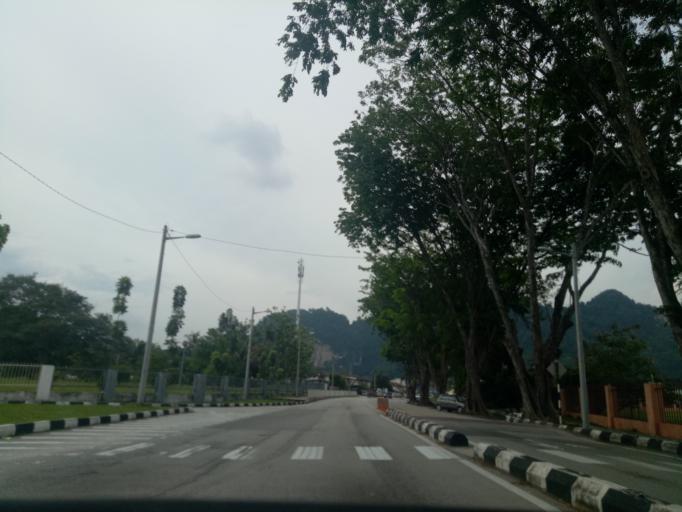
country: MY
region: Perak
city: Ipoh
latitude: 4.5934
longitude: 101.1235
